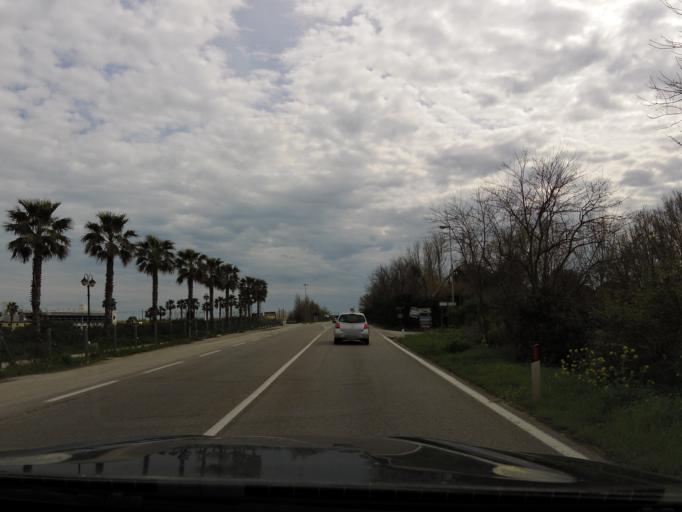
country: IT
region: The Marches
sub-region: Provincia di Macerata
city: Porto Potenza Picena
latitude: 43.3921
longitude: 13.6815
